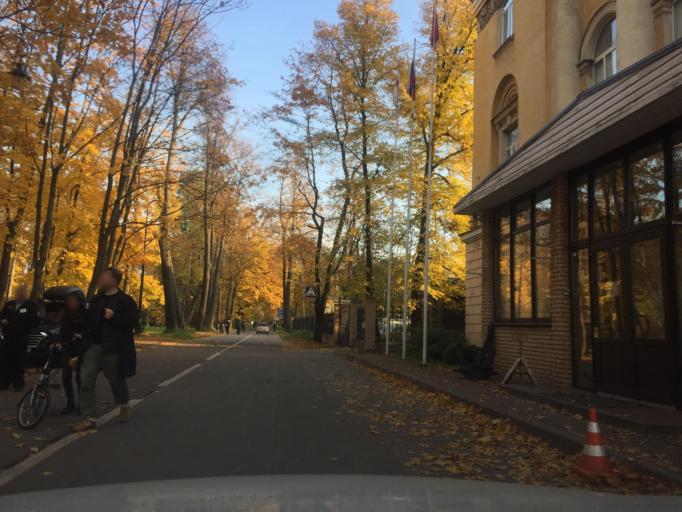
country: RU
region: St.-Petersburg
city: Novaya Derevnya
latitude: 59.9801
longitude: 30.2805
